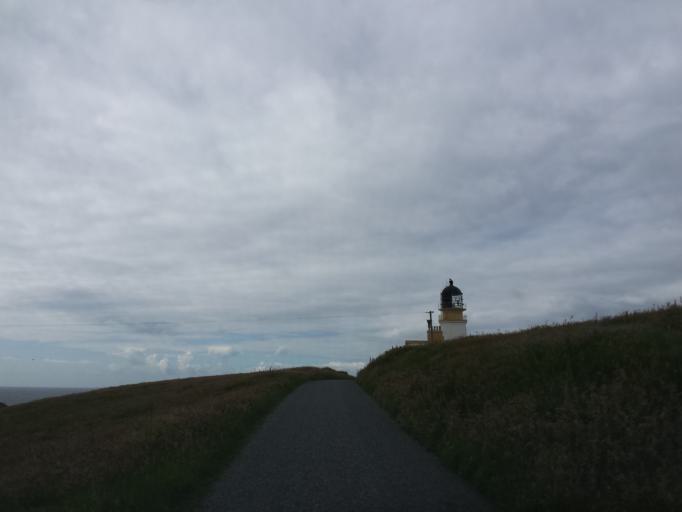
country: GB
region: Scotland
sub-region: Dumfries and Galloway
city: Stranraer
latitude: 54.8628
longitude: -5.1457
